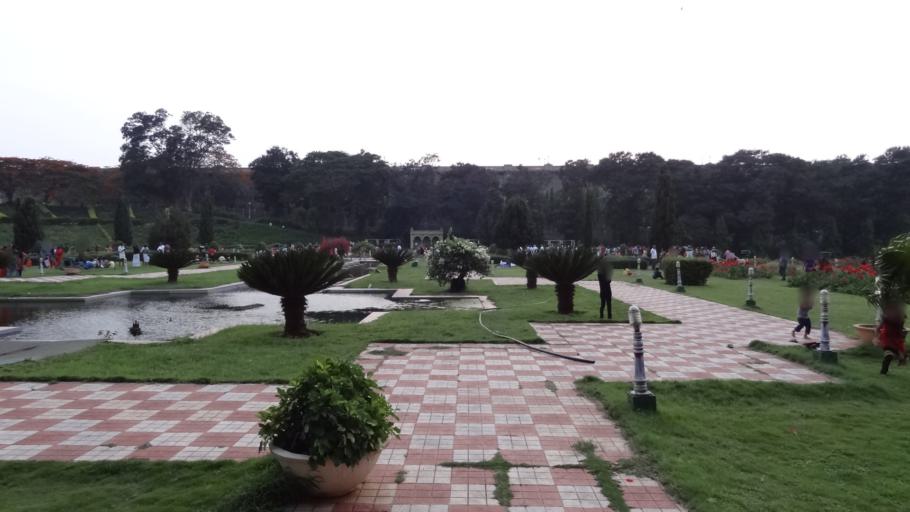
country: IN
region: Karnataka
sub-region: Mandya
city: Shrirangapattana
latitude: 12.4206
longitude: 76.5734
